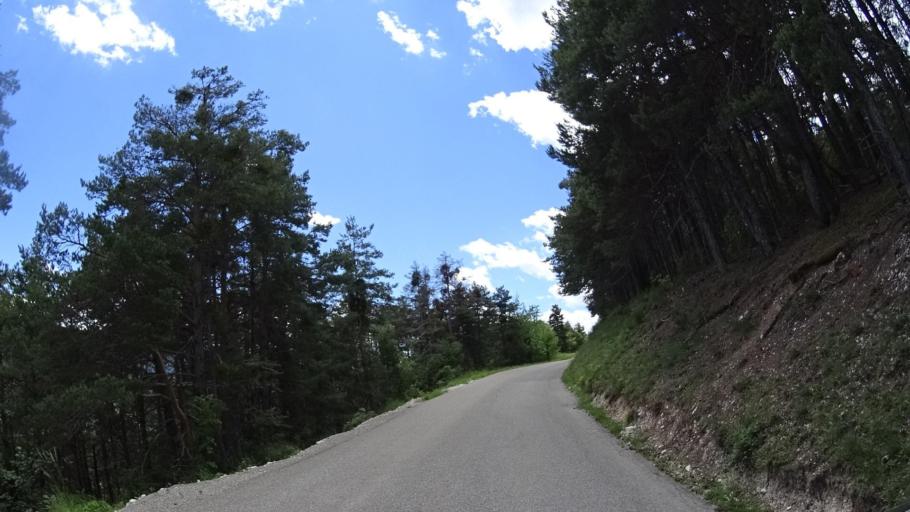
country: FR
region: Provence-Alpes-Cote d'Azur
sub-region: Departement des Alpes-de-Haute-Provence
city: Annot
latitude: 44.0172
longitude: 6.6280
